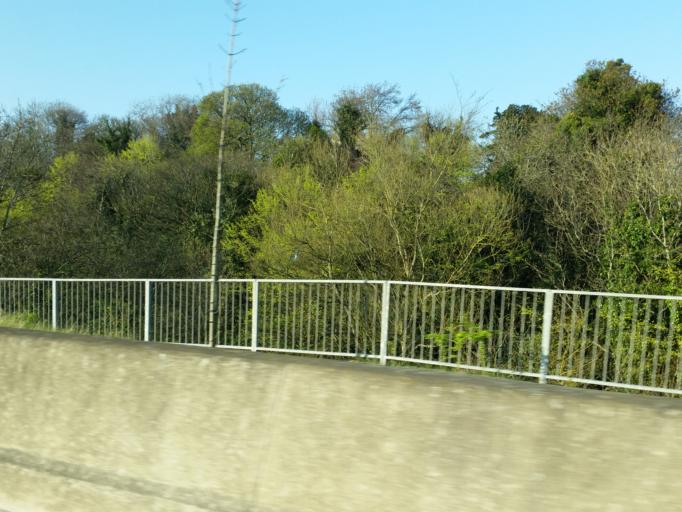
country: IE
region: Leinster
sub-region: Fingal County
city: Blanchardstown
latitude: 53.3897
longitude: -6.3695
